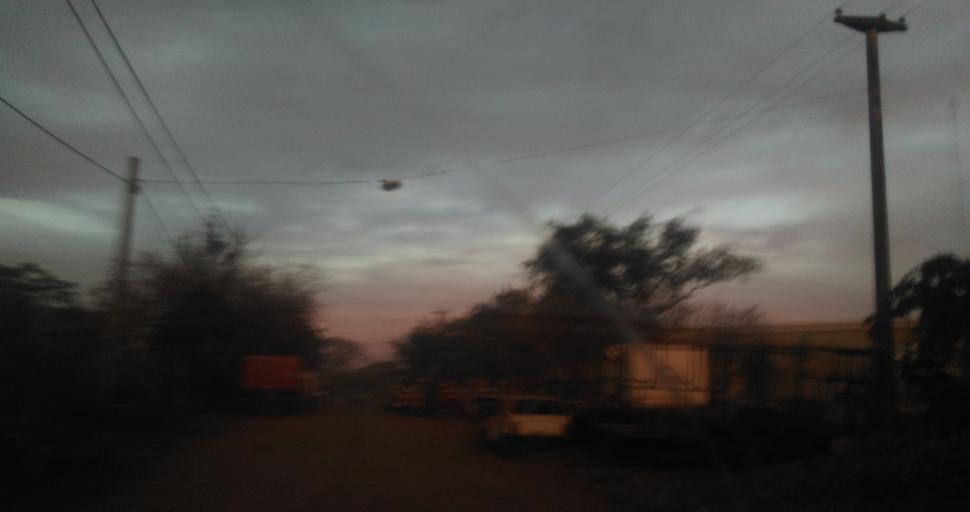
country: AR
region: Chaco
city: Fontana
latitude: -27.4341
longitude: -59.0127
